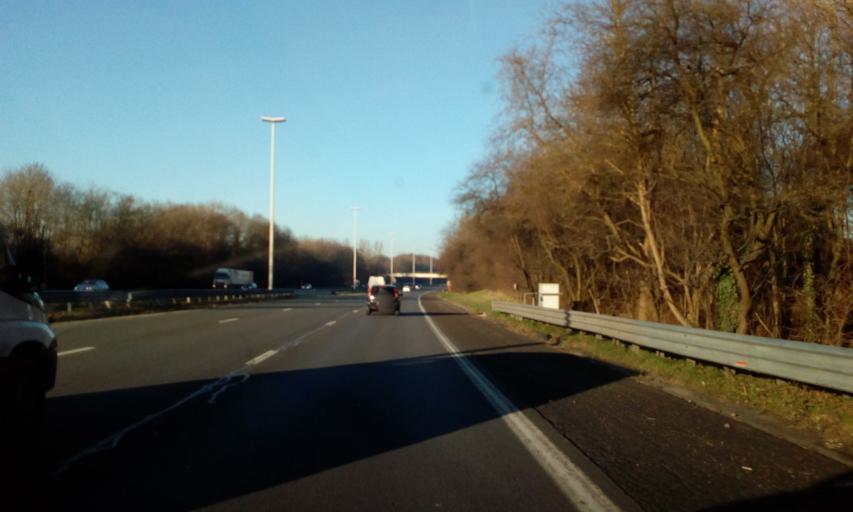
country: BE
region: Wallonia
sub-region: Province du Brabant Wallon
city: Nivelles
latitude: 50.6011
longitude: 4.2965
